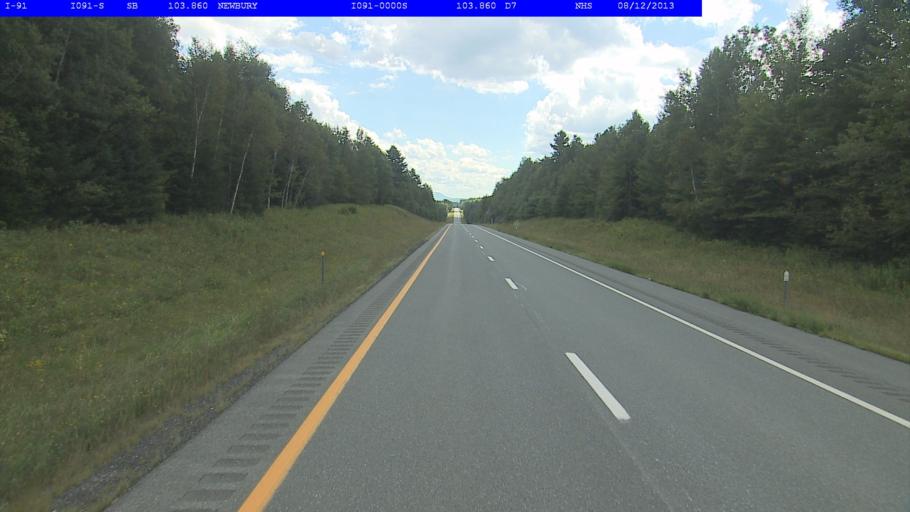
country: US
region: New Hampshire
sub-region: Grafton County
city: Haverhill
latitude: 44.0694
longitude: -72.1113
